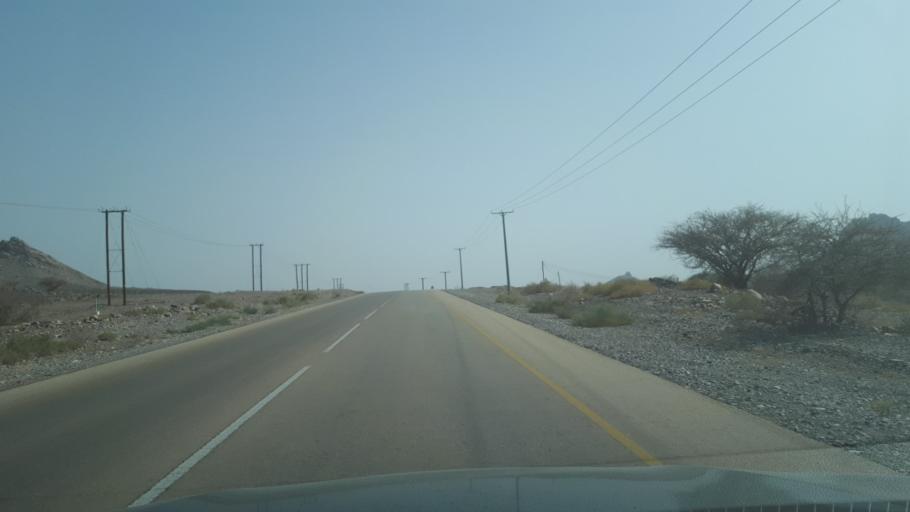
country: OM
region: Az Zahirah
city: `Ibri
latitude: 23.1877
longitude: 56.9231
